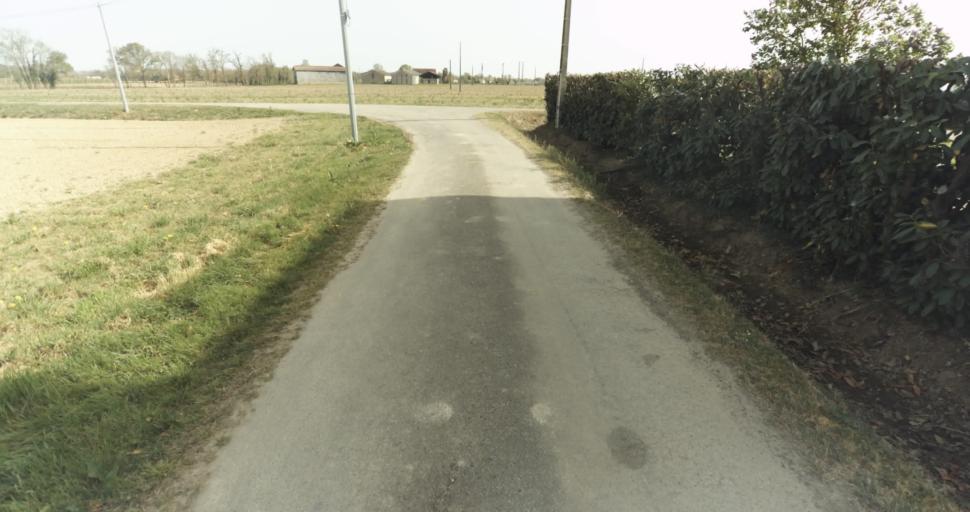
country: FR
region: Midi-Pyrenees
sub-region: Departement du Tarn-et-Garonne
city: Moissac
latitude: 44.0813
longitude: 1.1084
